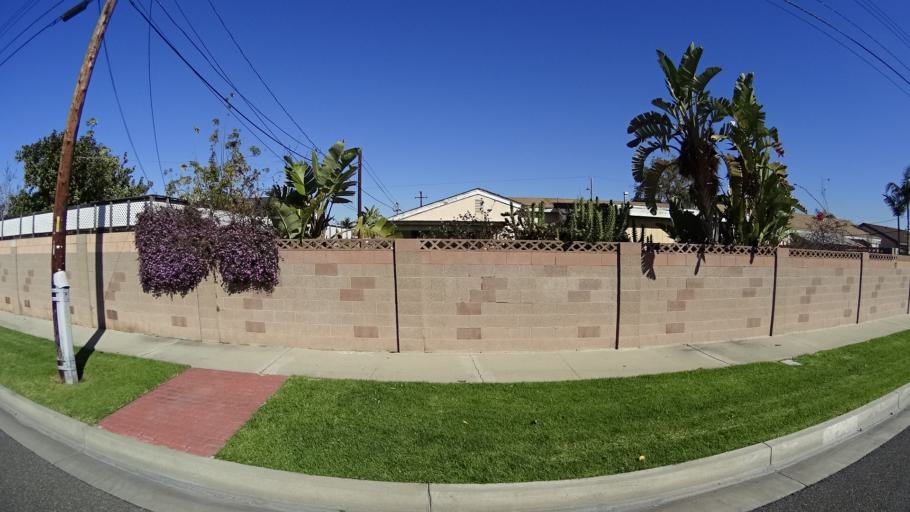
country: US
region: California
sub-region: Orange County
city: Cypress
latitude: 33.8184
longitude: -118.0204
